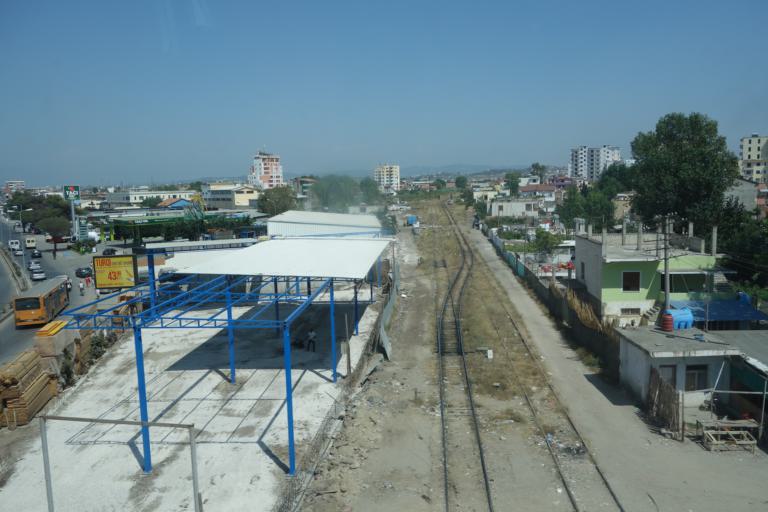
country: AL
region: Durres
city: Durres
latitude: 41.3169
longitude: 19.4704
